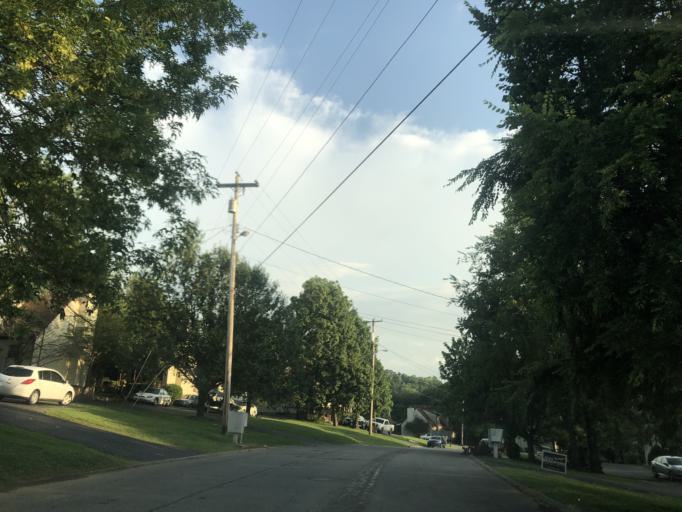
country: US
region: Tennessee
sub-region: Davidson County
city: Lakewood
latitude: 36.1365
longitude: -86.6382
